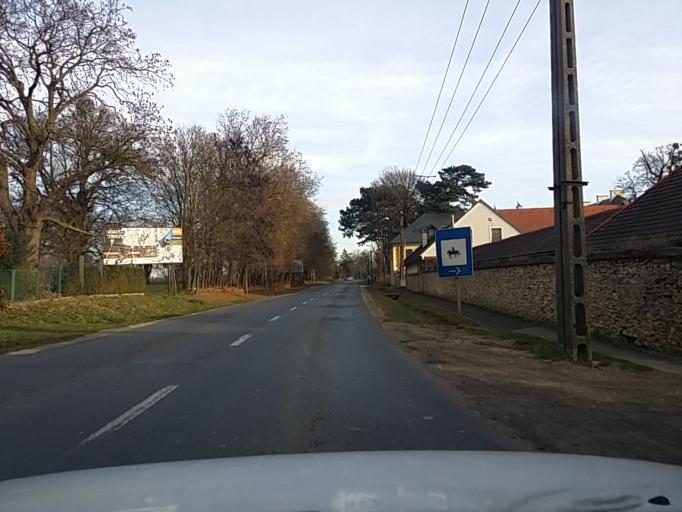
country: HU
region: Veszprem
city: Urkut
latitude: 46.9896
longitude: 17.6973
